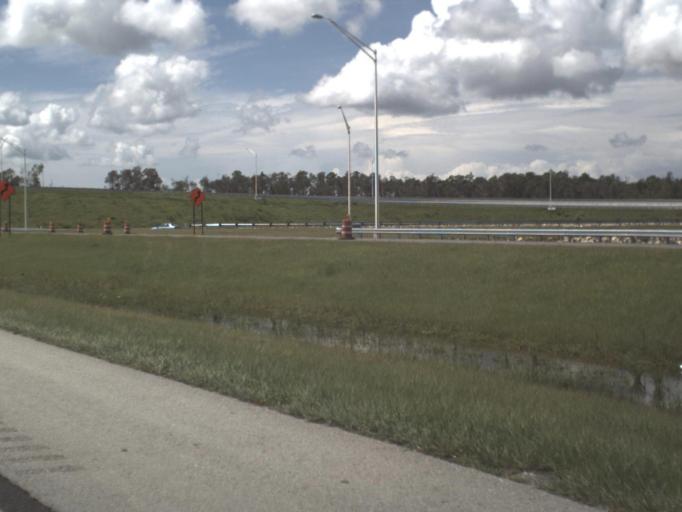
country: US
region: Florida
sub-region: Lee County
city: Three Oaks
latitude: 26.5140
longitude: -81.7948
